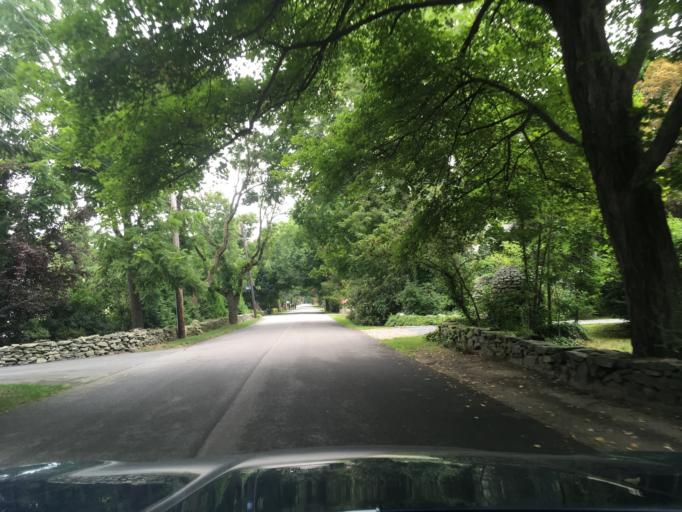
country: US
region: Rhode Island
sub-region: Bristol County
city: Warren
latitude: 41.7123
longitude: -71.3038
